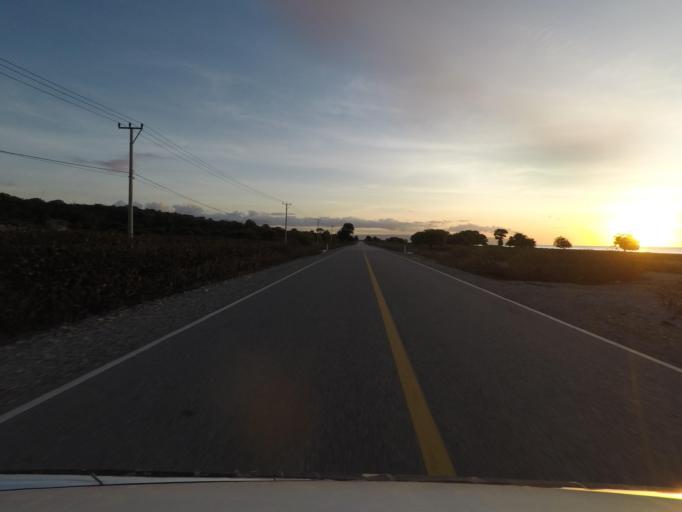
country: TL
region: Baucau
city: Baucau
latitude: -8.4528
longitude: 126.6325
